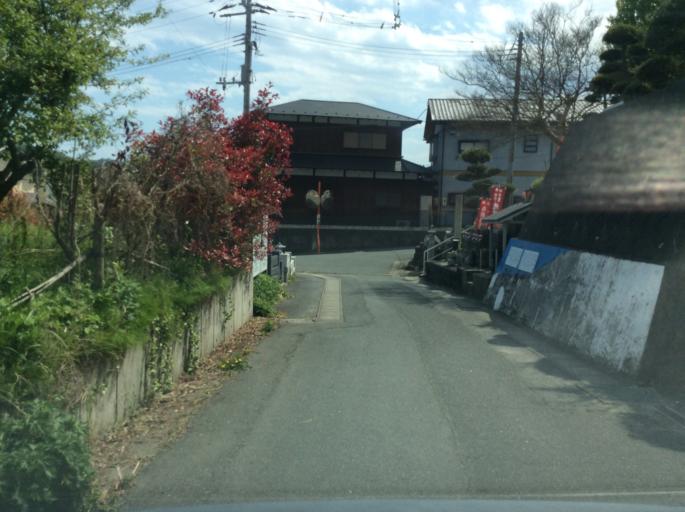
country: JP
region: Ibaraki
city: Kitaibaraki
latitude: 36.8846
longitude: 140.7855
